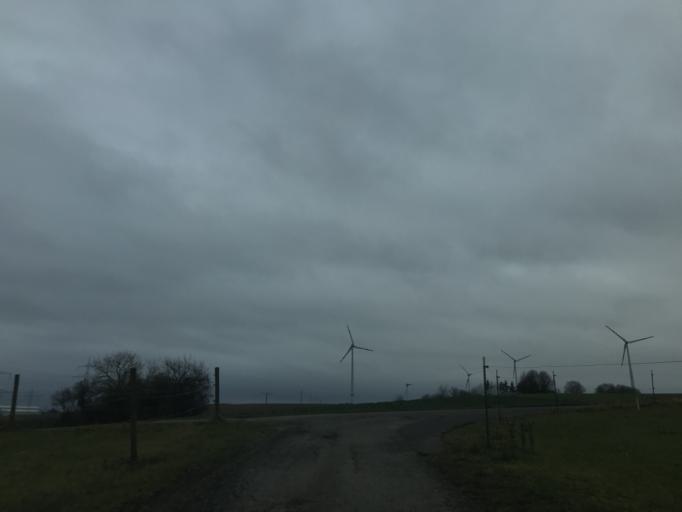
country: DE
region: Rheinland-Pfalz
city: Trierweiler
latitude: 49.7872
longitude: 6.5699
